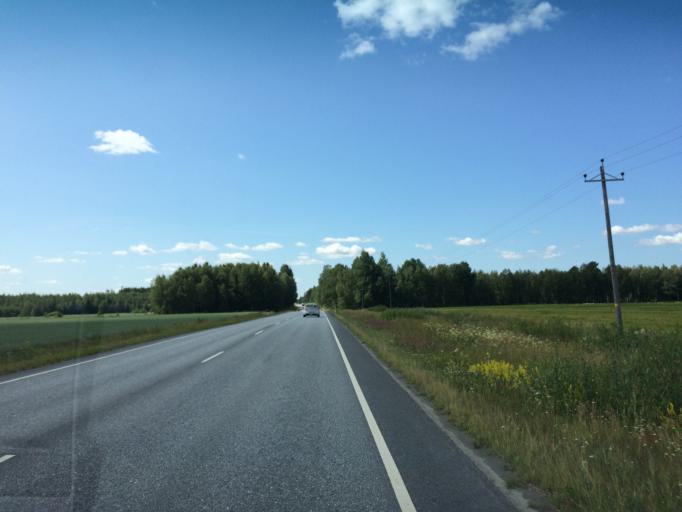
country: FI
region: Pirkanmaa
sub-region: Lounais-Pirkanmaa
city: Kiikoinen
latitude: 61.4855
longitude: 22.6565
